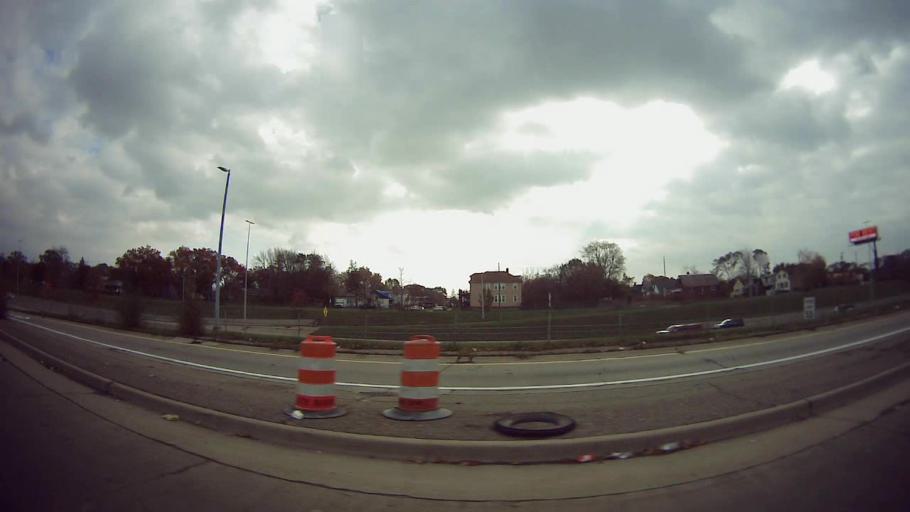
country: US
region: Michigan
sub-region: Wayne County
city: Highland Park
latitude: 42.4053
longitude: -83.1382
